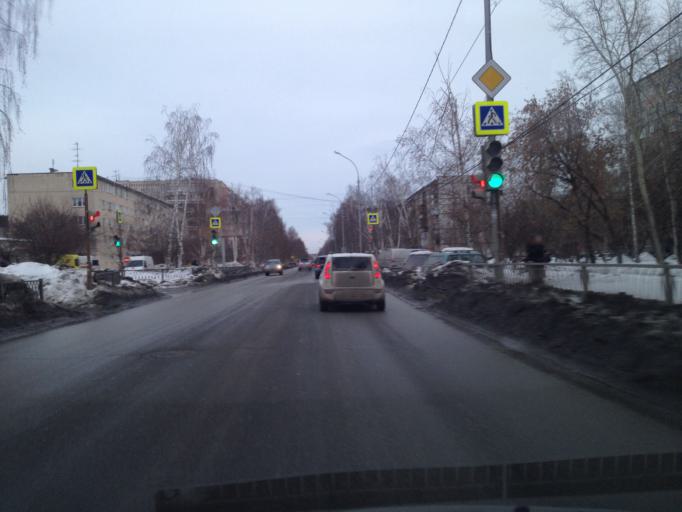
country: RU
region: Sverdlovsk
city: Sovkhoznyy
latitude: 56.8081
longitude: 60.5516
